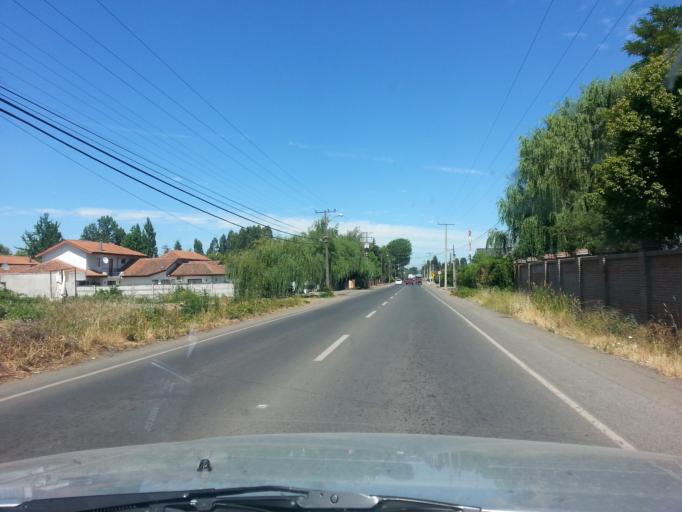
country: CL
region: Biobio
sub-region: Provincia de Nuble
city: Chillan
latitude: -36.5893
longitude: -72.0611
